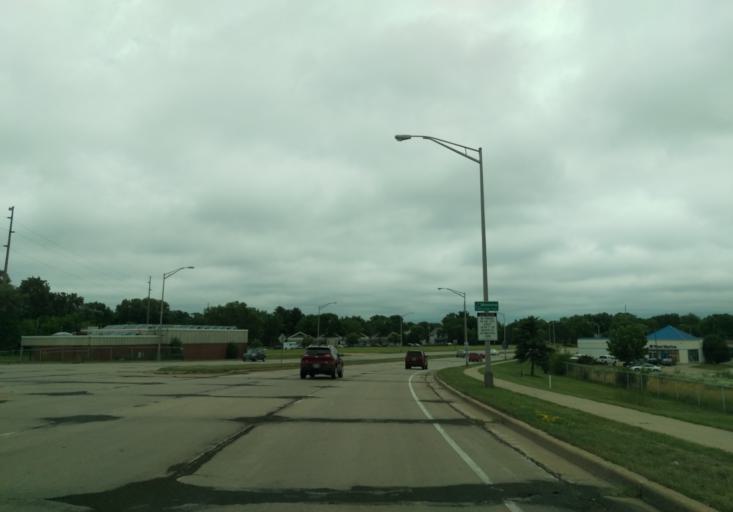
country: US
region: Wisconsin
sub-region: Dane County
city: Monona
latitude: 43.0447
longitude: -89.3540
